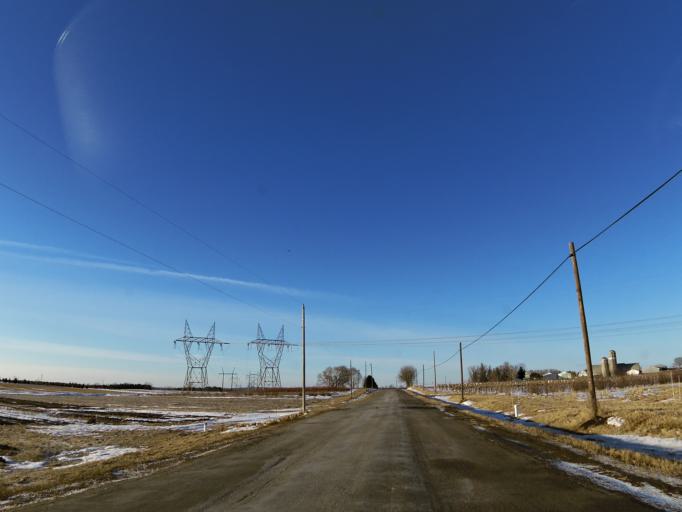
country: US
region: Minnesota
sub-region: Washington County
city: Cottage Grove
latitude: 44.8136
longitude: -92.8814
